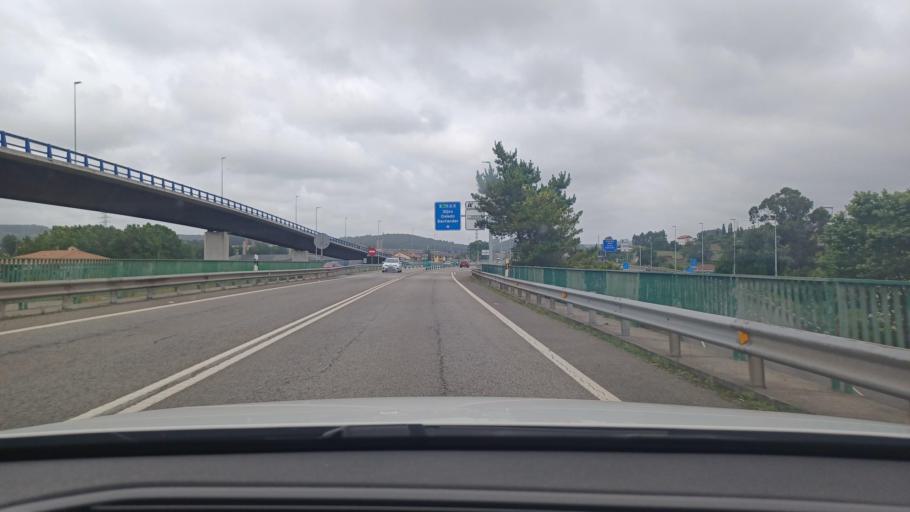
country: ES
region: Asturias
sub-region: Province of Asturias
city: Aviles
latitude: 43.5512
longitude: -5.9007
